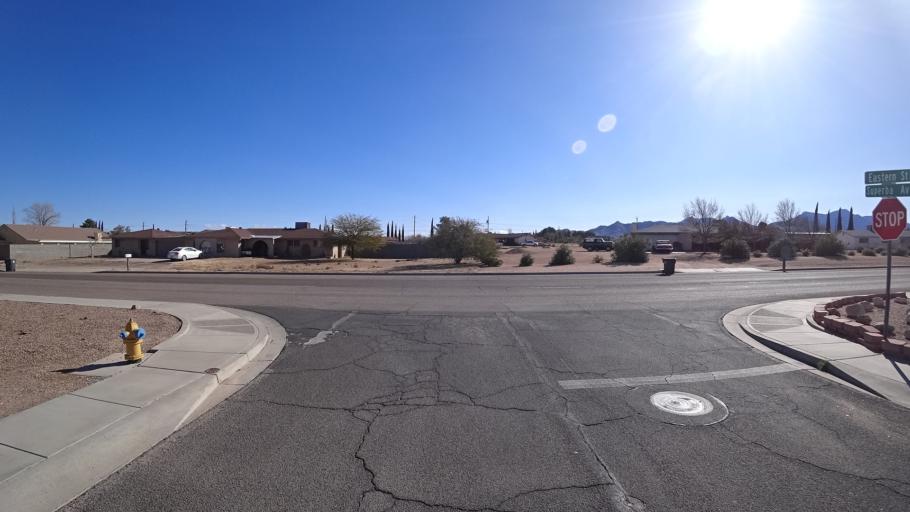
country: US
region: Arizona
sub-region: Mohave County
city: Kingman
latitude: 35.2021
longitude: -114.0116
